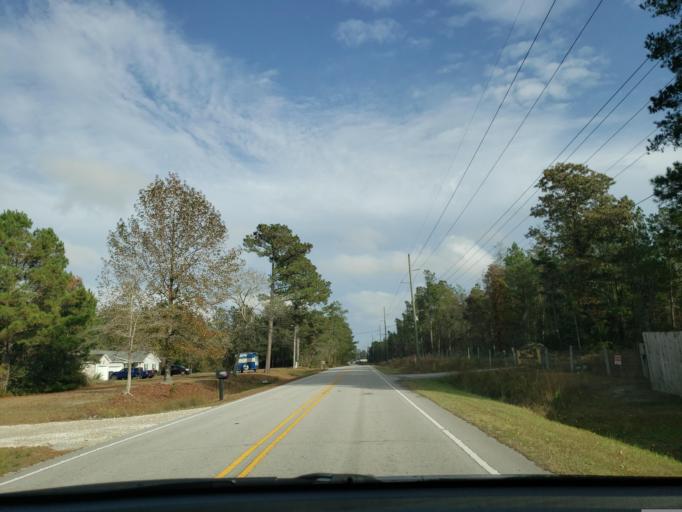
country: US
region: North Carolina
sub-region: Onslow County
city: Jacksonville
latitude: 34.6860
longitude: -77.5202
